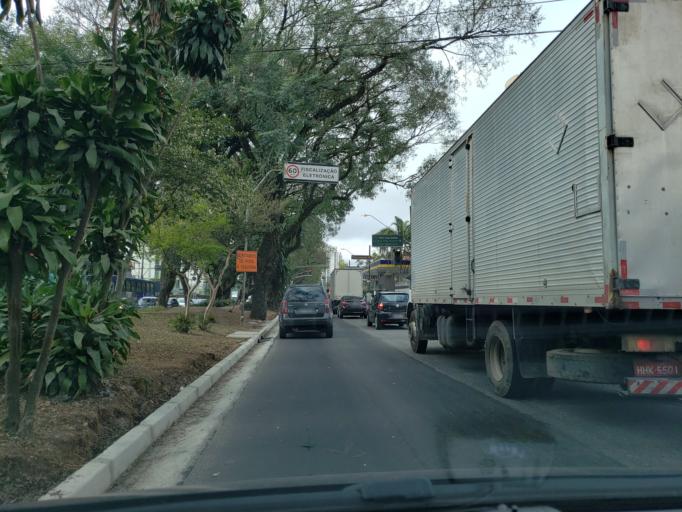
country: BR
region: Sao Paulo
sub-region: Santo Andre
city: Santo Andre
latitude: -23.6459
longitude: -46.5430
